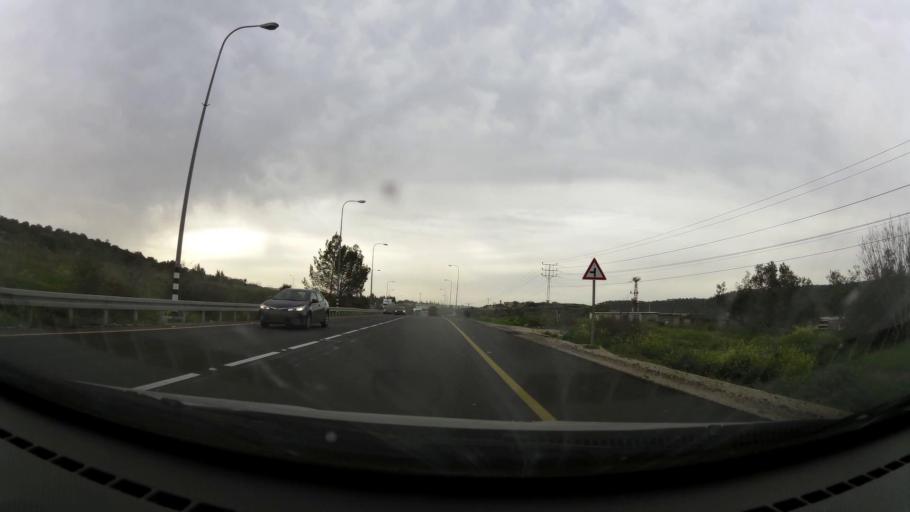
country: IL
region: Jerusalem
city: Bet Shemesh
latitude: 31.6765
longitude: 35.0055
